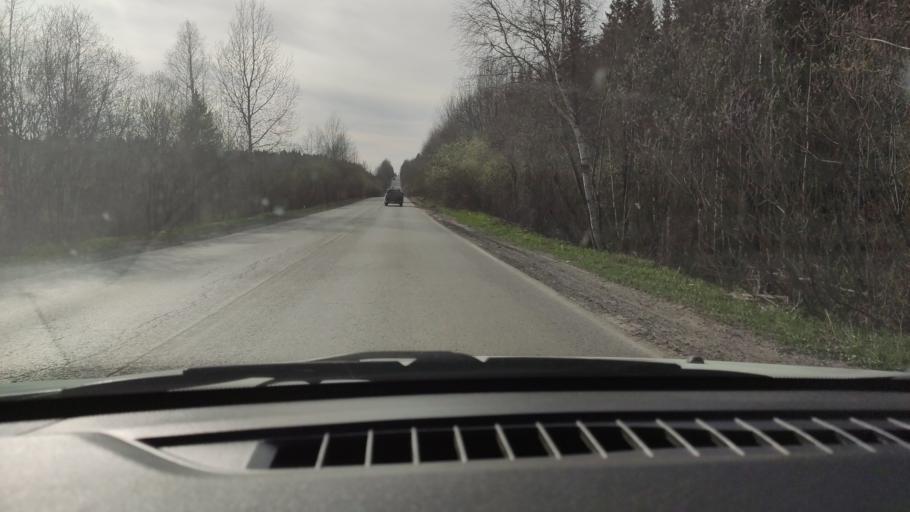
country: RU
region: Perm
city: Ferma
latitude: 57.9356
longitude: 56.4712
